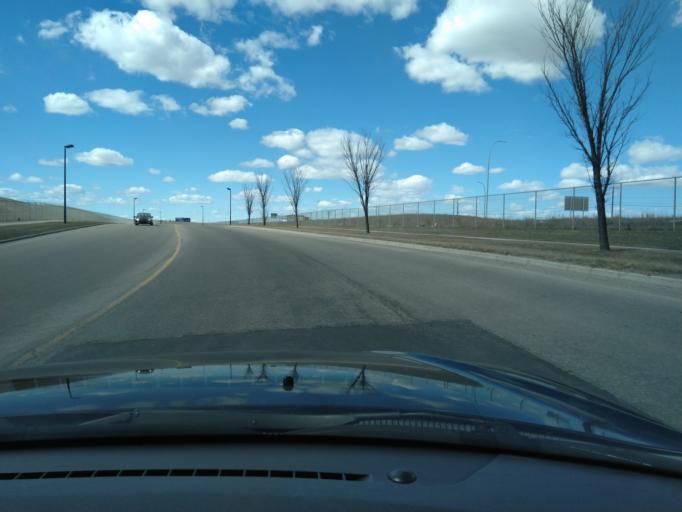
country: CA
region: Alberta
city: Calgary
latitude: 51.1388
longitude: -114.0170
